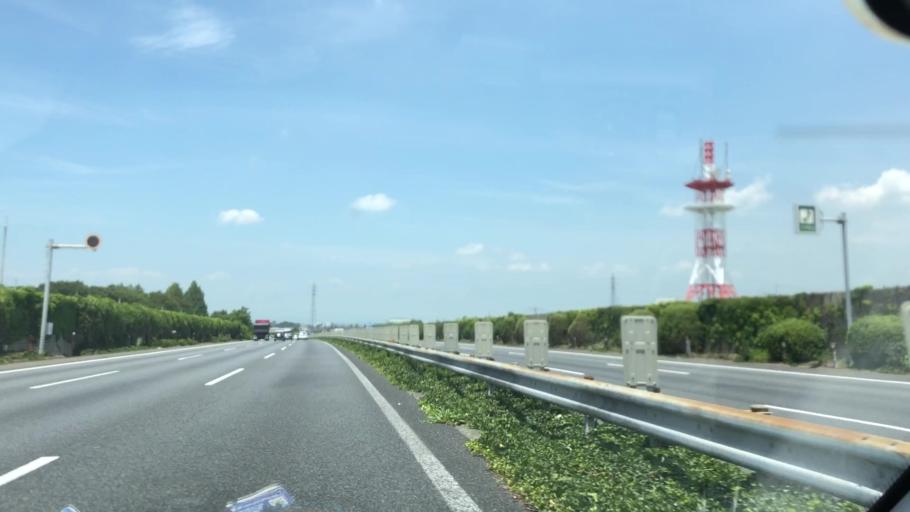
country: JP
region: Saitama
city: Kazo
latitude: 36.1098
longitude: 139.6376
